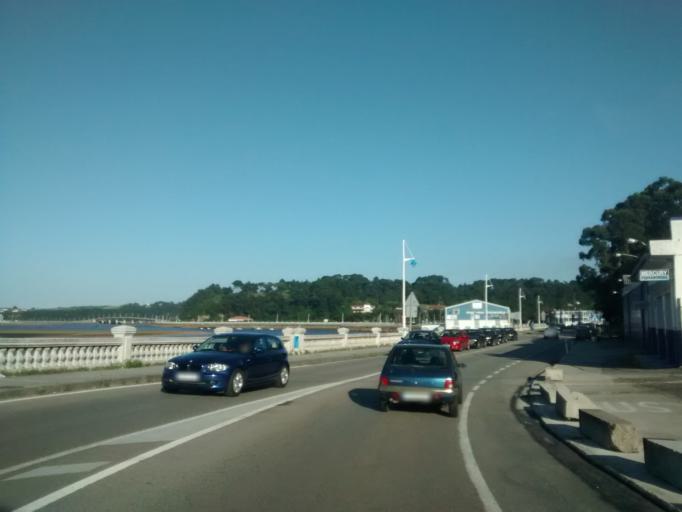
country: ES
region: Cantabria
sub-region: Provincia de Cantabria
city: Santander
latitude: 43.4485
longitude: -3.7692
